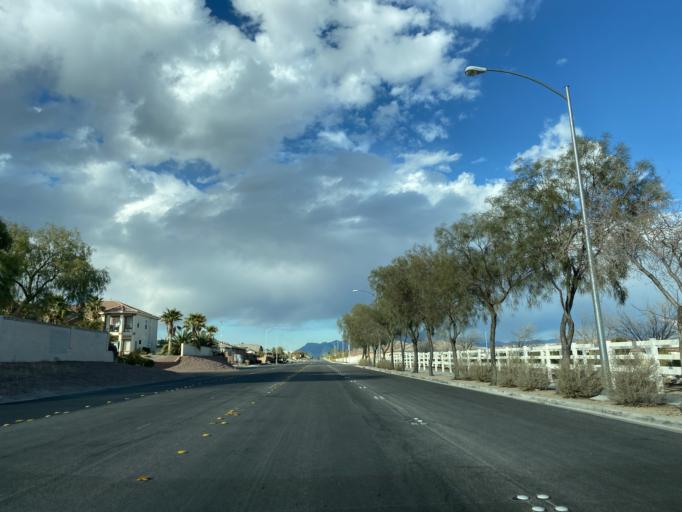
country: US
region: Nevada
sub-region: Clark County
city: Summerlin South
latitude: 36.2818
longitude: -115.3058
